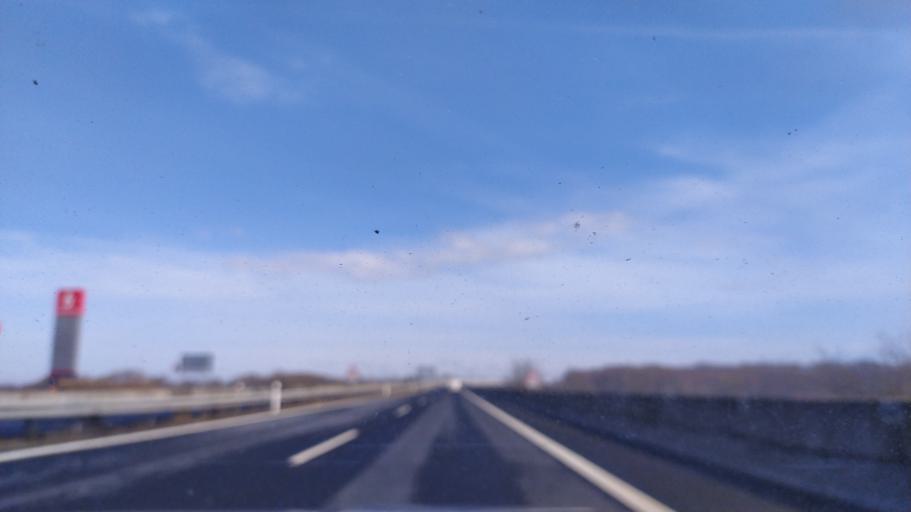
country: CZ
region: Karlovarsky
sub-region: Okres Cheb
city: Cheb
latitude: 50.1003
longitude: 12.3854
